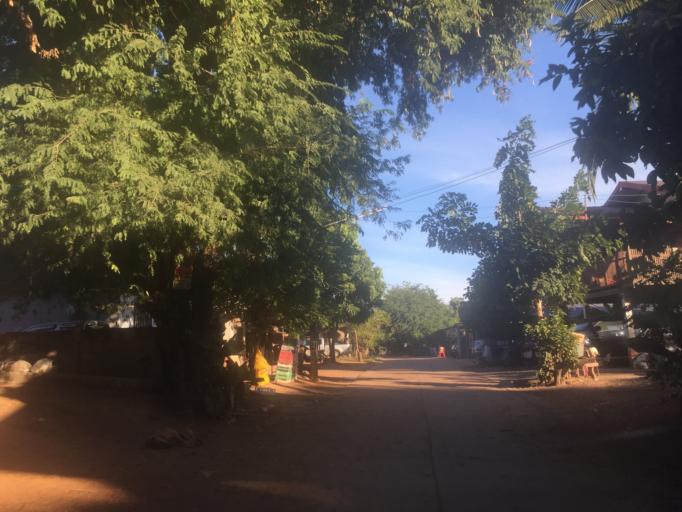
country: TH
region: Changwat Udon Thani
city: Si That
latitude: 16.9689
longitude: 103.2300
